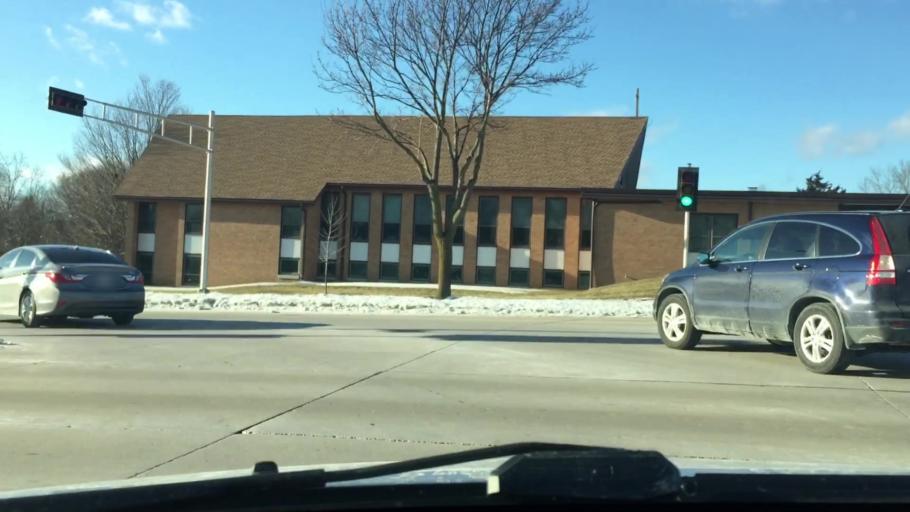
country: US
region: Wisconsin
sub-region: Milwaukee County
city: Greenfield
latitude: 42.9886
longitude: -88.0561
